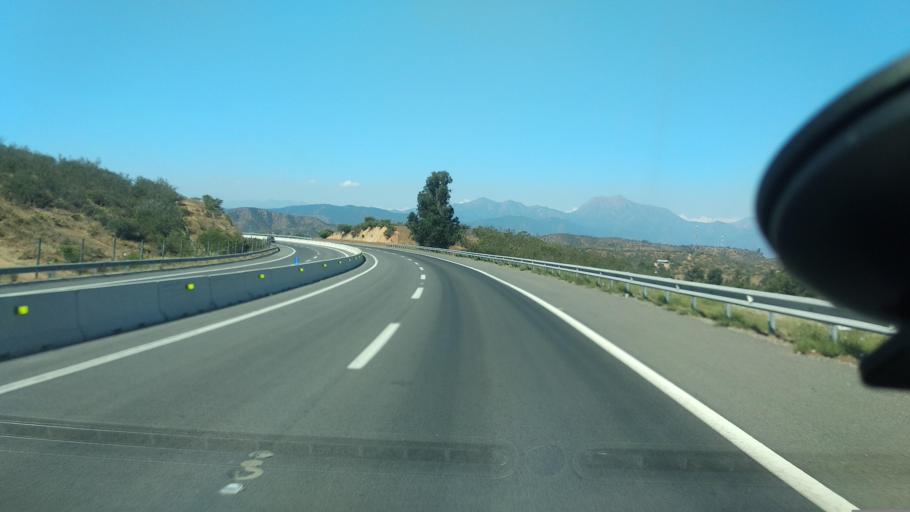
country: CL
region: Valparaiso
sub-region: Provincia de Marga Marga
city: Villa Alemana
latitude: -33.0437
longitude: -71.3205
